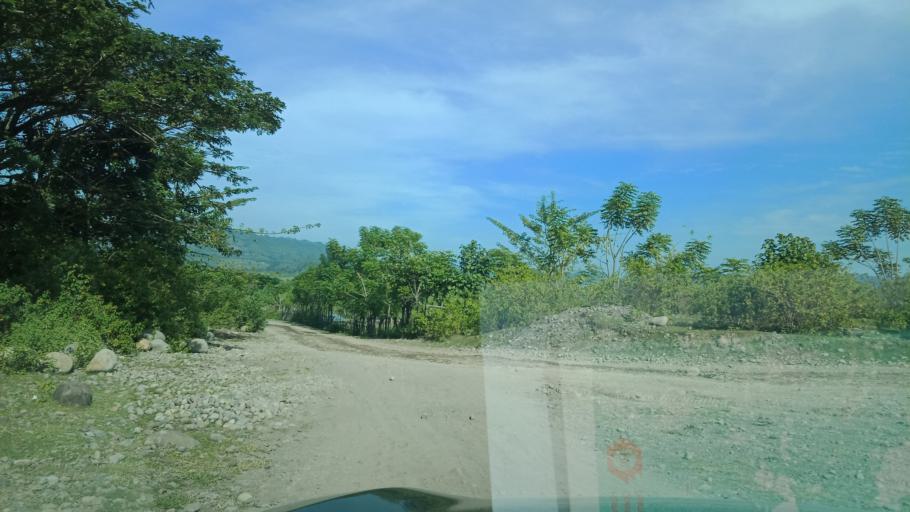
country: ID
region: South Sulawesi
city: Makassar
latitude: -5.2556
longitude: 119.6431
